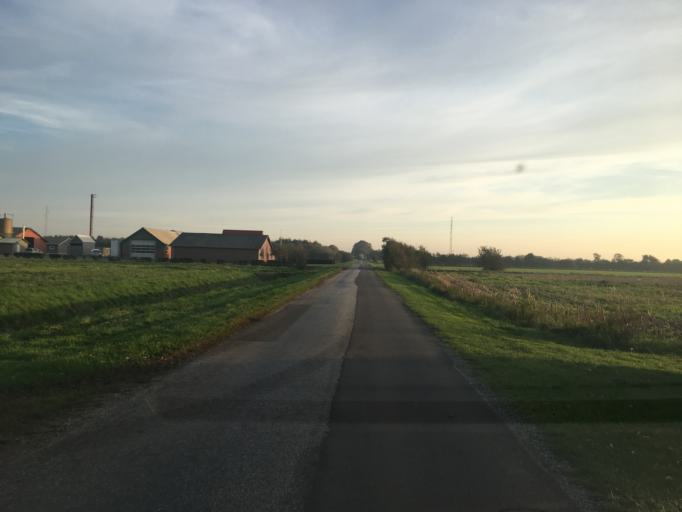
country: DK
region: South Denmark
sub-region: Tonder Kommune
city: Logumkloster
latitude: 55.0544
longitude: 9.0239
